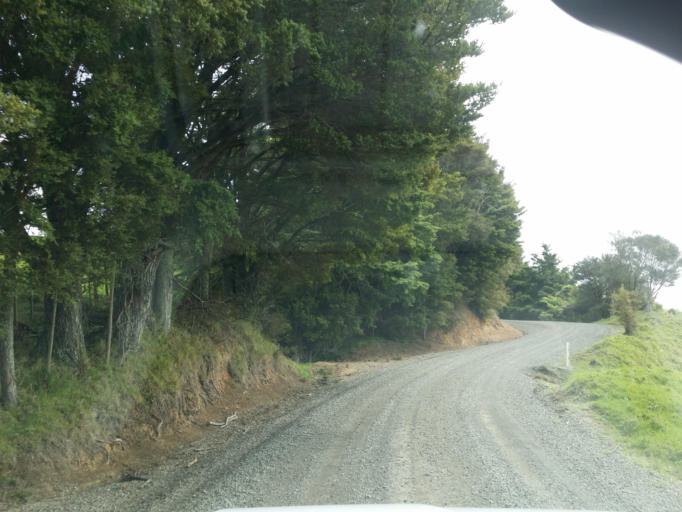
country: NZ
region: Northland
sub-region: Kaipara District
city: Dargaville
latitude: -35.9203
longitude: 174.0796
